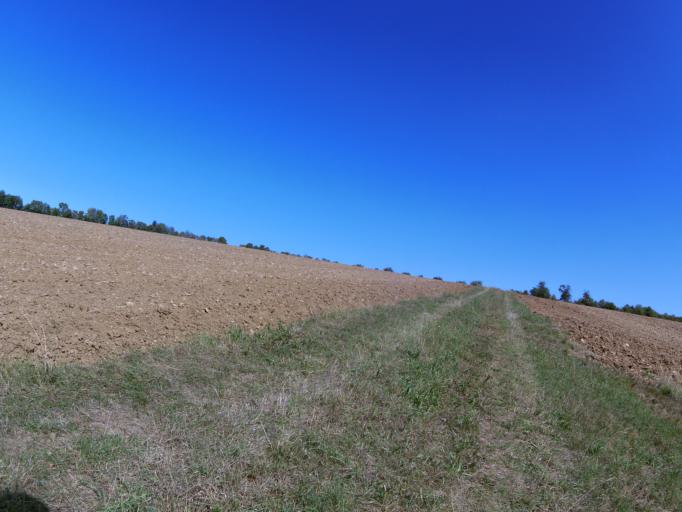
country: DE
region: Bavaria
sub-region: Regierungsbezirk Unterfranken
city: Waldbrunn
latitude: 49.7541
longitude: 9.7921
